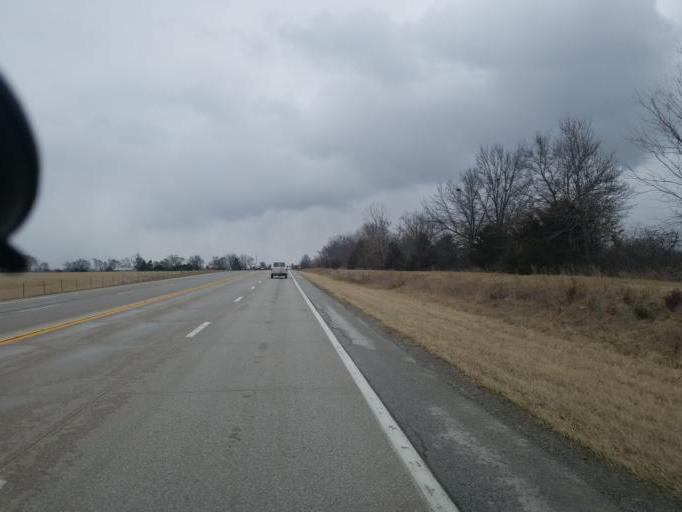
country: US
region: Missouri
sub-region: Macon County
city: Macon
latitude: 39.7803
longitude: -92.4793
